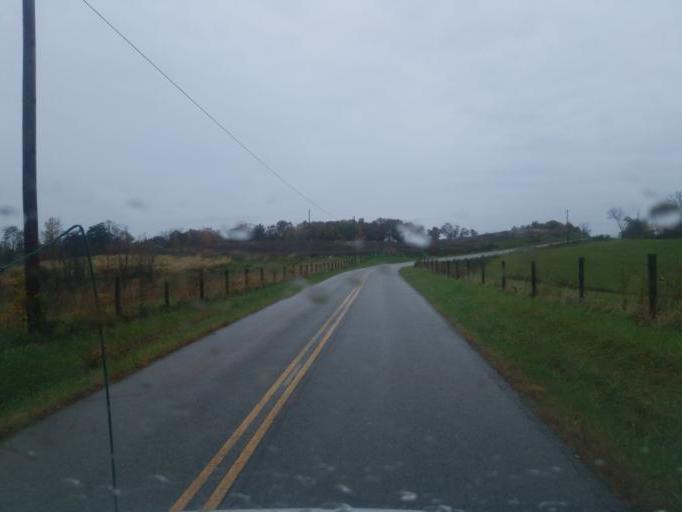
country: US
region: Ohio
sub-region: Washington County
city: Beverly
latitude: 39.4543
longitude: -81.6162
